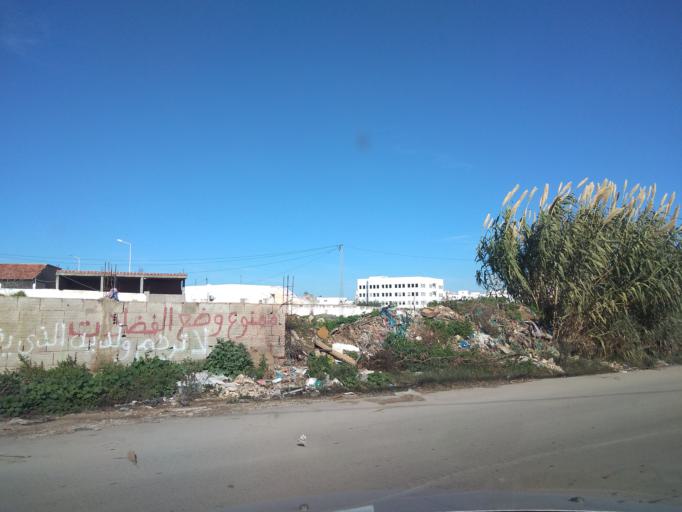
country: TN
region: Manouba
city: Manouba
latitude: 36.8006
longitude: 10.0896
